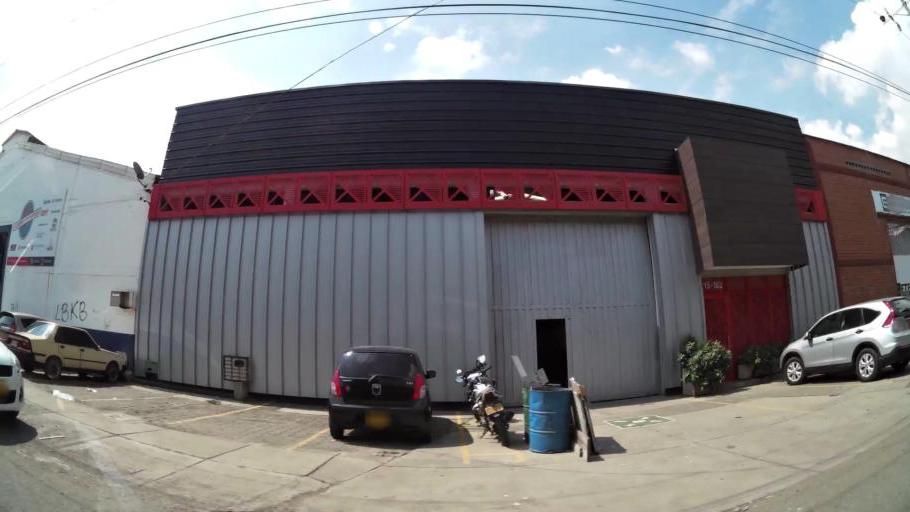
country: CO
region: Valle del Cauca
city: Cali
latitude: 3.4922
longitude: -76.5079
